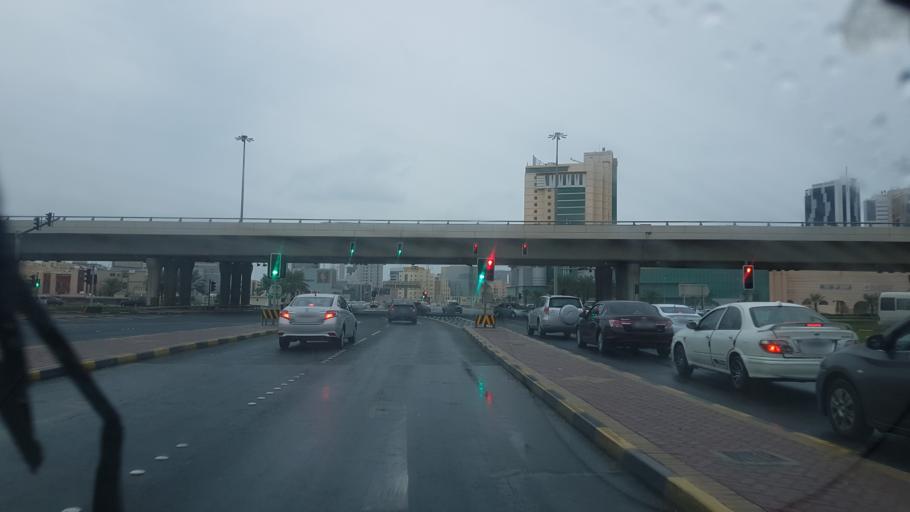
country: BH
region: Manama
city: Jidd Hafs
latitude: 26.2298
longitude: 50.5351
